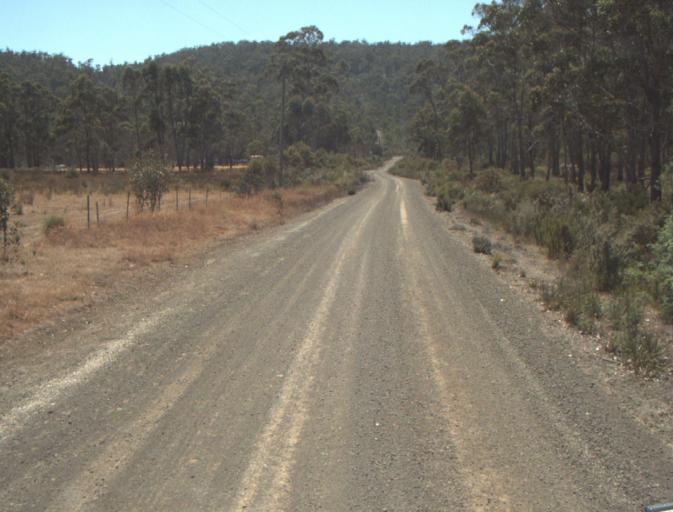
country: AU
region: Tasmania
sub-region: Launceston
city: Mayfield
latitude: -41.2768
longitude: 147.0986
